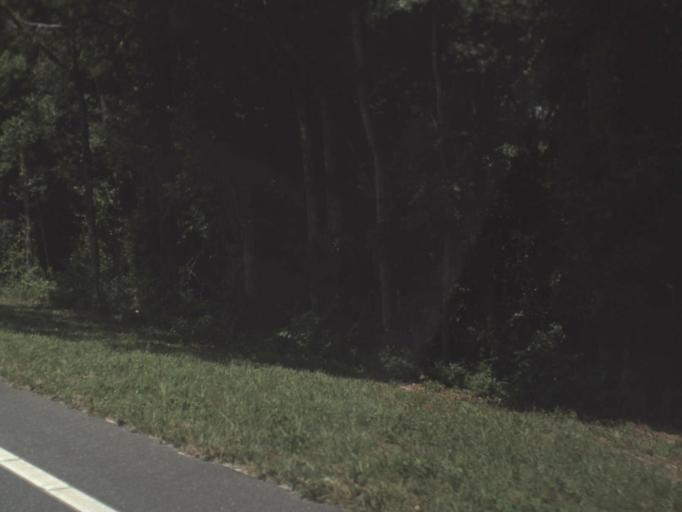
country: US
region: Florida
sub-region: Alachua County
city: High Springs
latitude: 29.9143
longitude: -82.8601
